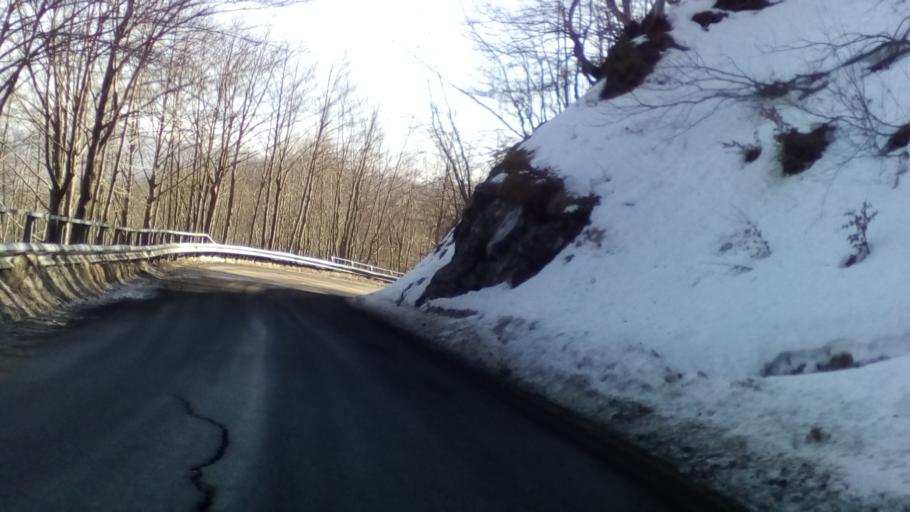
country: IT
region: Tuscany
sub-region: Provincia di Lucca
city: Fosciandora
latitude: 44.1987
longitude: 10.5026
